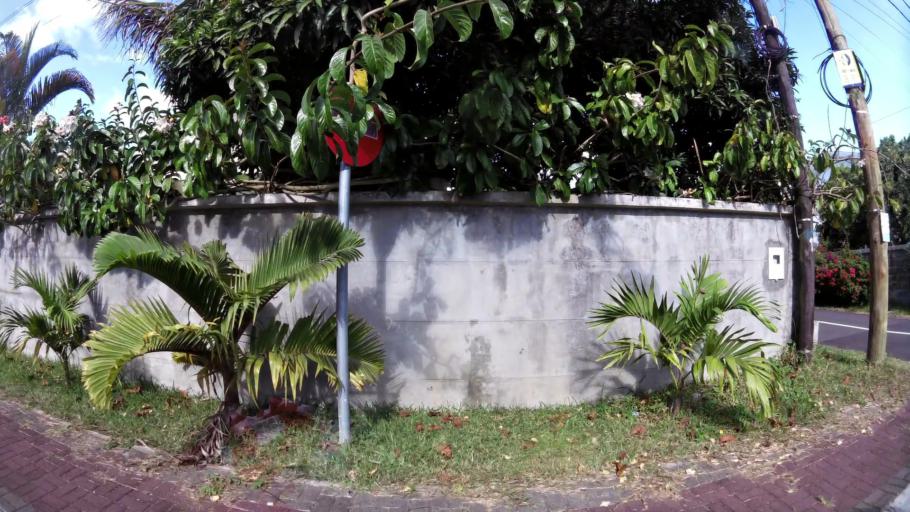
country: MU
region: Plaines Wilhems
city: Quatre Bornes
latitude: -20.2703
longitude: 57.4868
